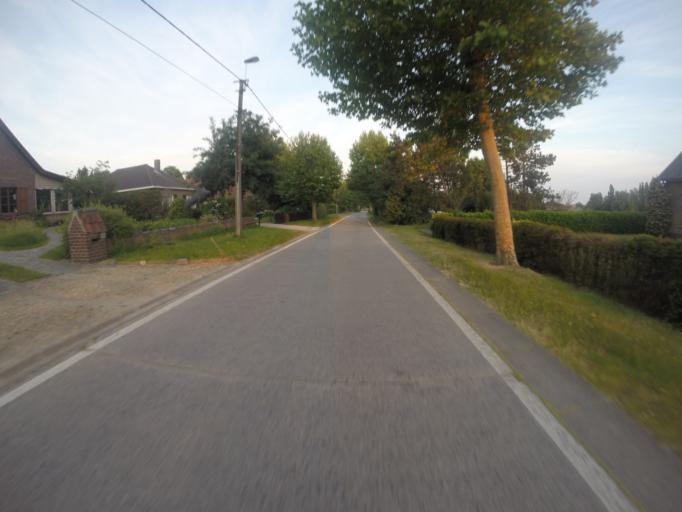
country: BE
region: Flanders
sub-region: Provincie Oost-Vlaanderen
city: Zomergem
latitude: 51.1200
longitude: 3.5364
